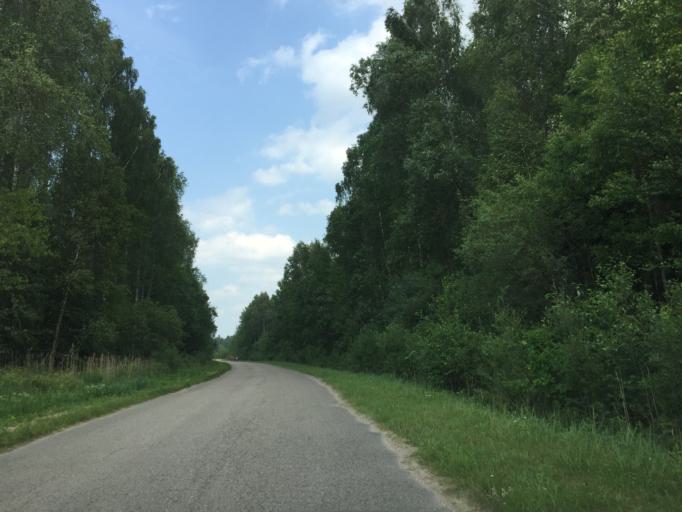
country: LV
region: Olaine
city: Olaine
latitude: 56.7802
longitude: 23.8749
